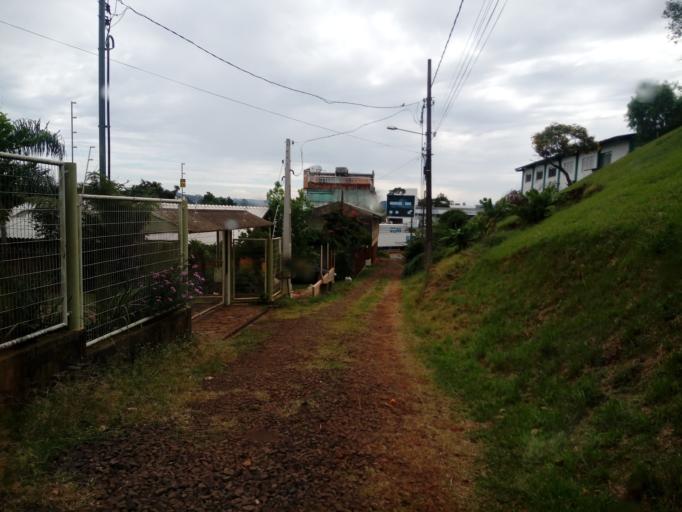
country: BR
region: Santa Catarina
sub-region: Chapeco
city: Chapeco
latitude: -27.0984
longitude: -52.6442
